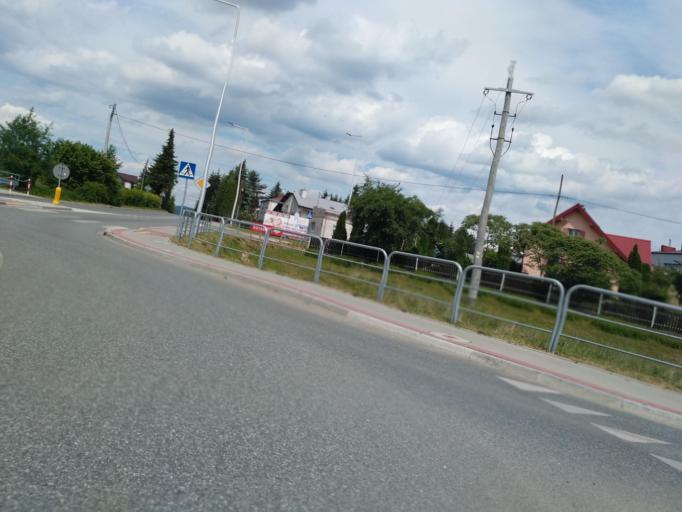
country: PL
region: Subcarpathian Voivodeship
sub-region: Powiat krosnienski
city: Odrzykon
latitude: 49.7048
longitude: 21.7245
